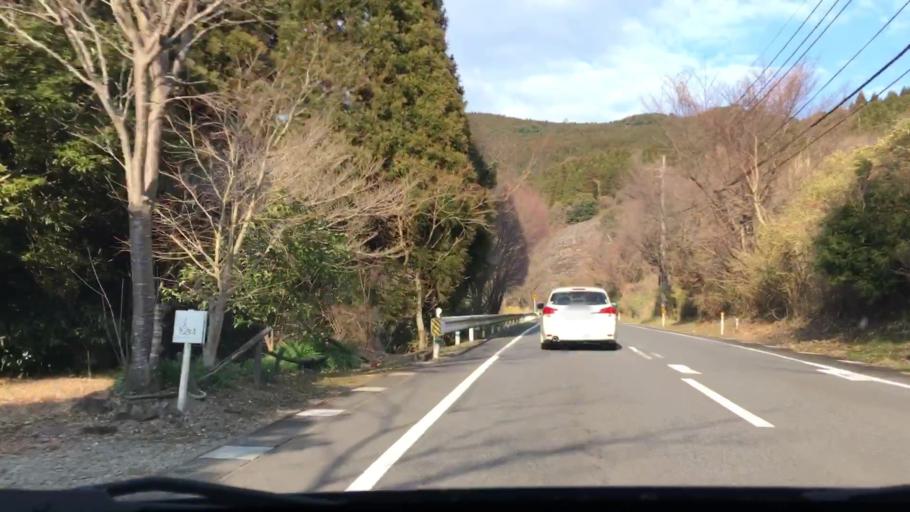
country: JP
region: Miyazaki
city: Miyazaki-shi
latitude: 31.7744
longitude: 131.3317
